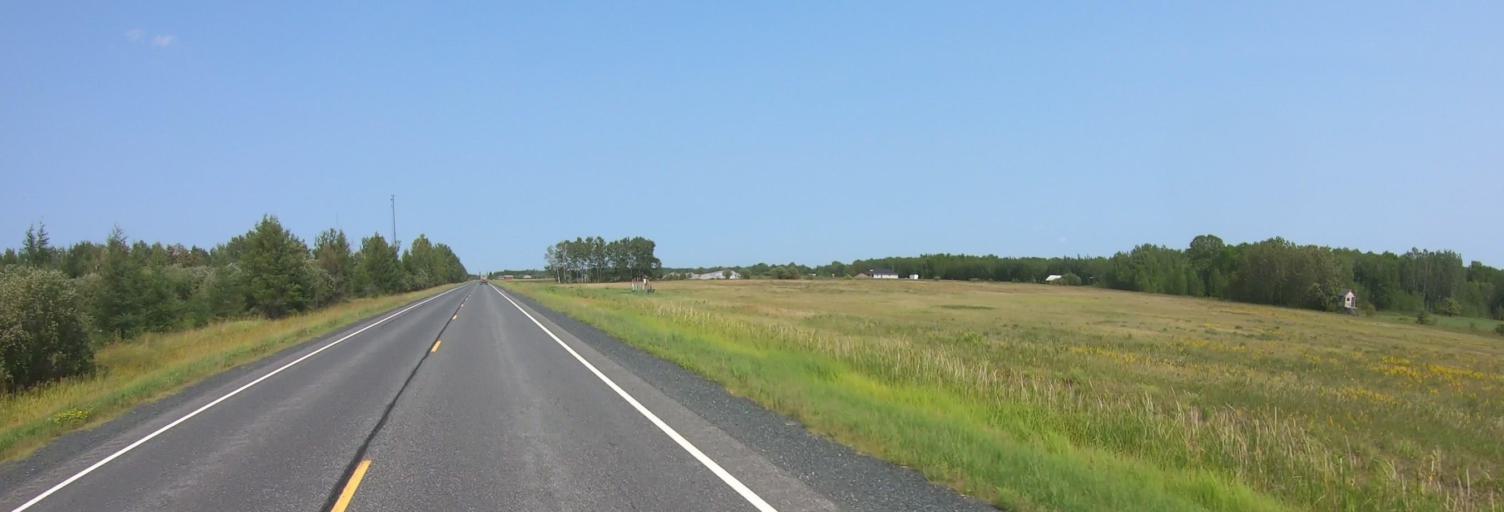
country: US
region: Minnesota
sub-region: Koochiching County
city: International Falls
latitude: 48.5431
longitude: -93.8183
